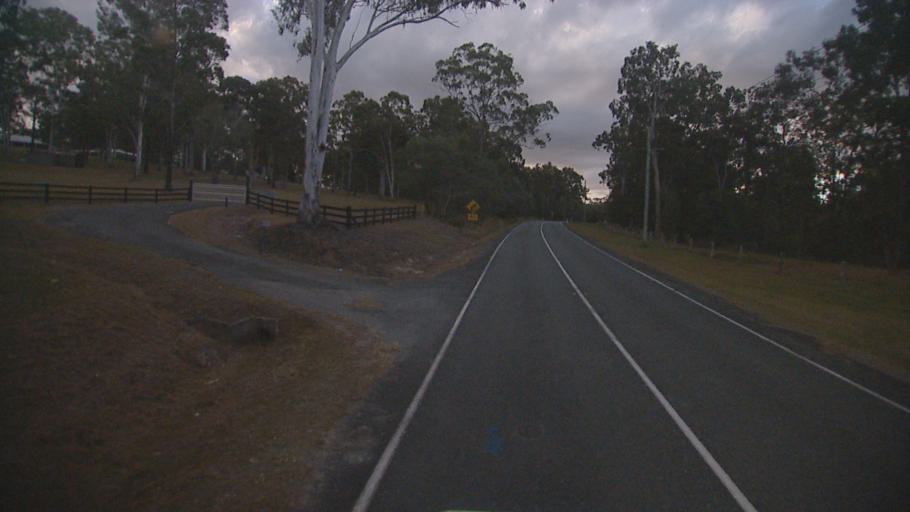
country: AU
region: Queensland
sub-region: Logan
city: Windaroo
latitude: -27.8100
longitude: 153.1549
